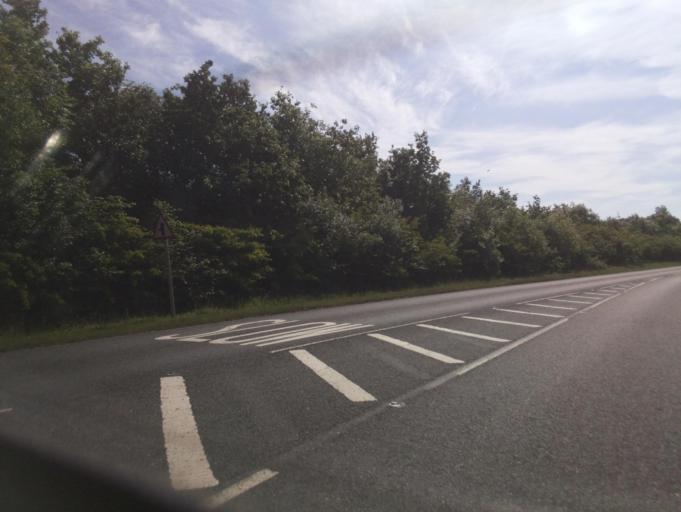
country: GB
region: England
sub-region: Lincolnshire
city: Skellingthorpe
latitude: 53.1662
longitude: -0.6408
